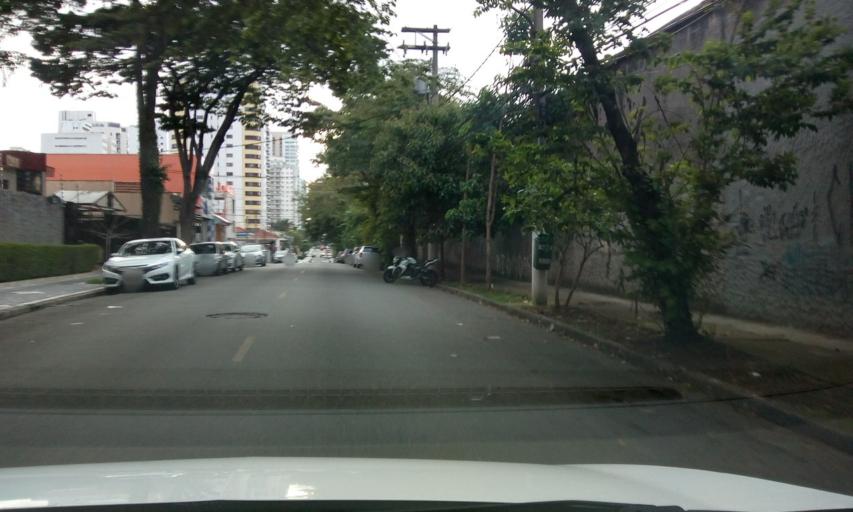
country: BR
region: Sao Paulo
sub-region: Sao Paulo
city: Sao Paulo
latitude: -23.5453
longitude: -46.5644
